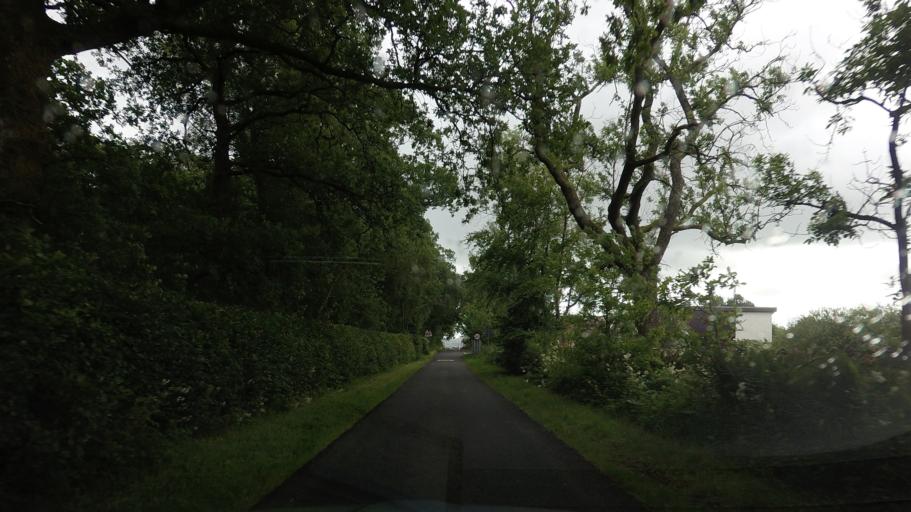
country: GB
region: Scotland
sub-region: Stirling
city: Killearn
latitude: 56.0707
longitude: -4.4509
